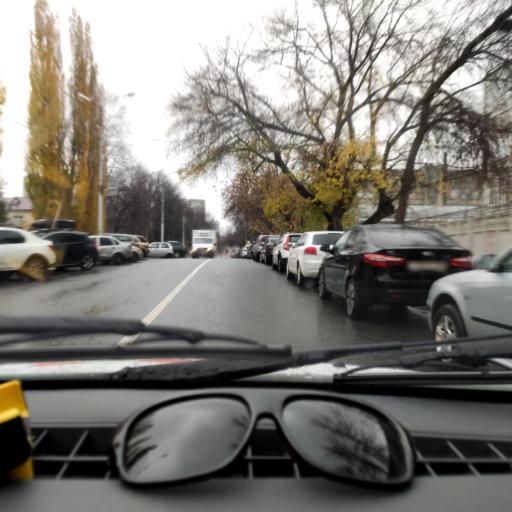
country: RU
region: Bashkortostan
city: Ufa
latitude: 54.7439
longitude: 55.9819
